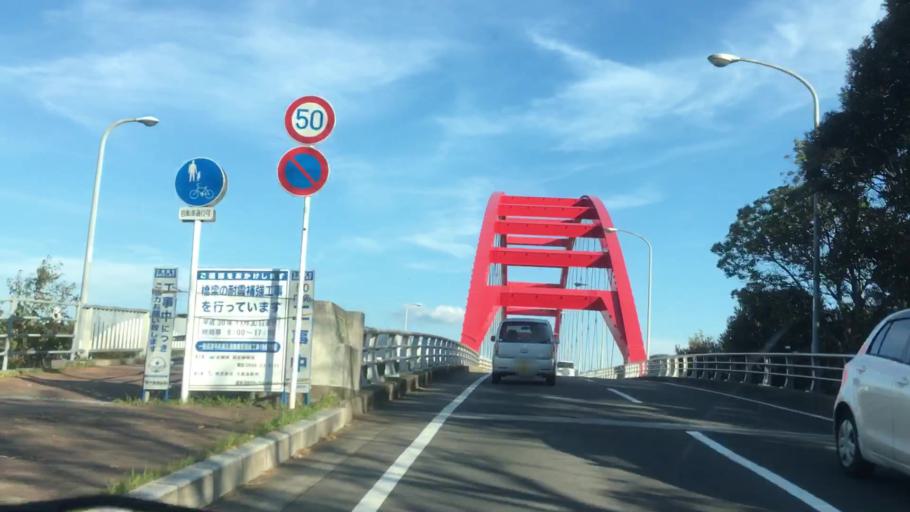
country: JP
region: Nagasaki
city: Sasebo
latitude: 33.0372
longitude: 129.6269
